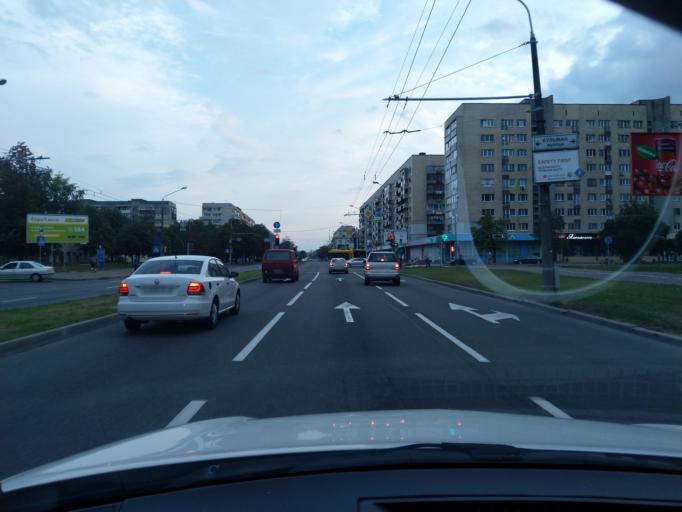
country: BY
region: Minsk
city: Minsk
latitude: 53.9270
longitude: 27.5724
